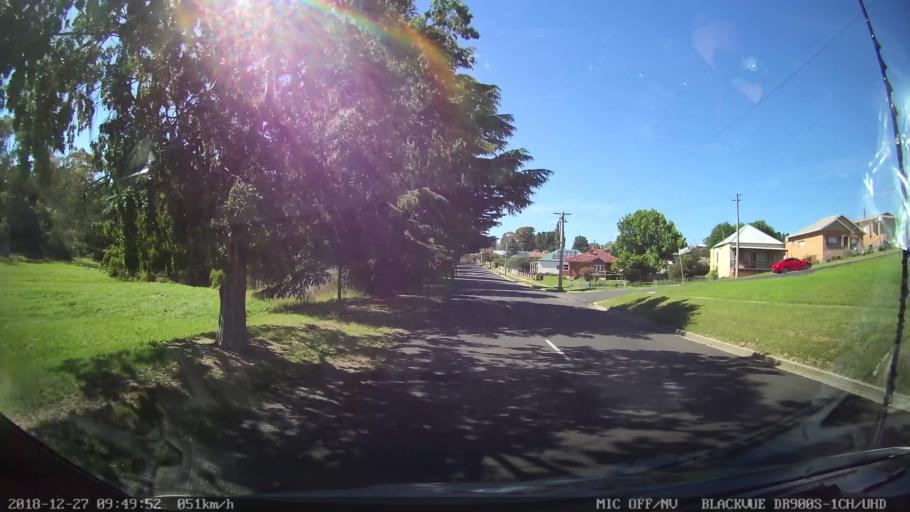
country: AU
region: New South Wales
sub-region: Lithgow
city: Portland
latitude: -33.3570
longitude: 149.9824
